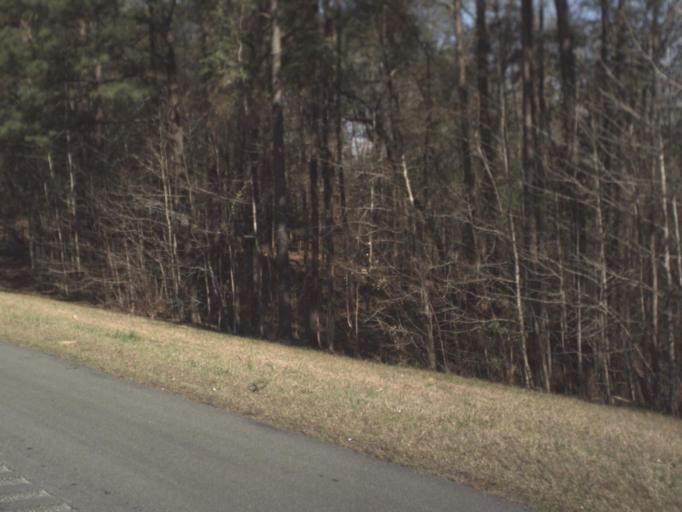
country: US
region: Florida
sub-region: Gadsden County
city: Chattahoochee
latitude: 30.6287
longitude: -84.8554
